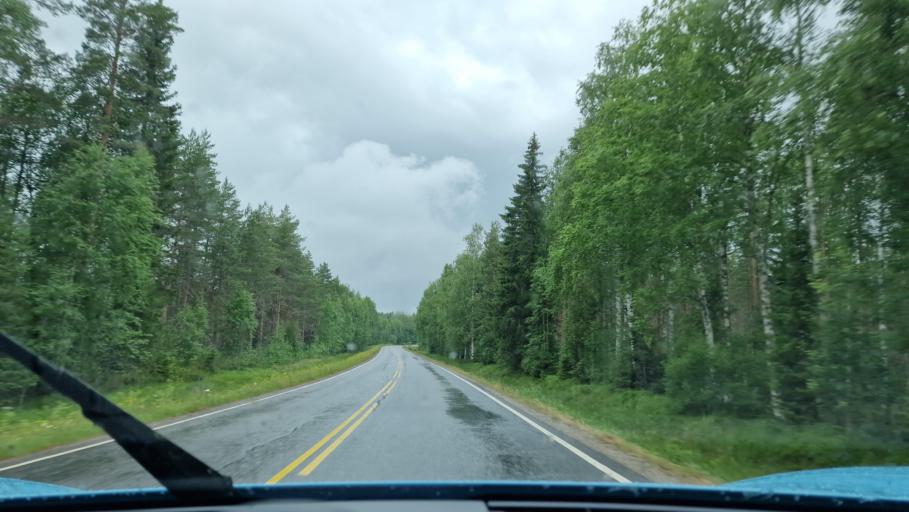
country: FI
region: Southern Ostrobothnia
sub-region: Jaerviseutu
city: Soini
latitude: 62.7900
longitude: 24.3817
